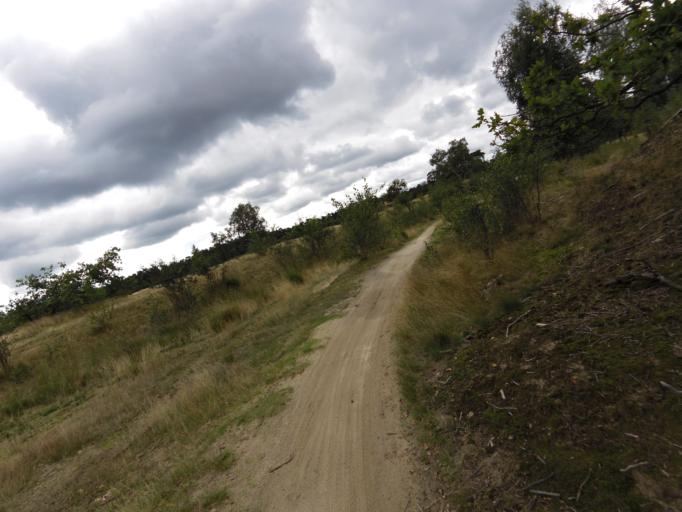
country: NL
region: North Brabant
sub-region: Gemeente Loon op Zand
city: Loon op Zand
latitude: 51.6453
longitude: 5.1418
